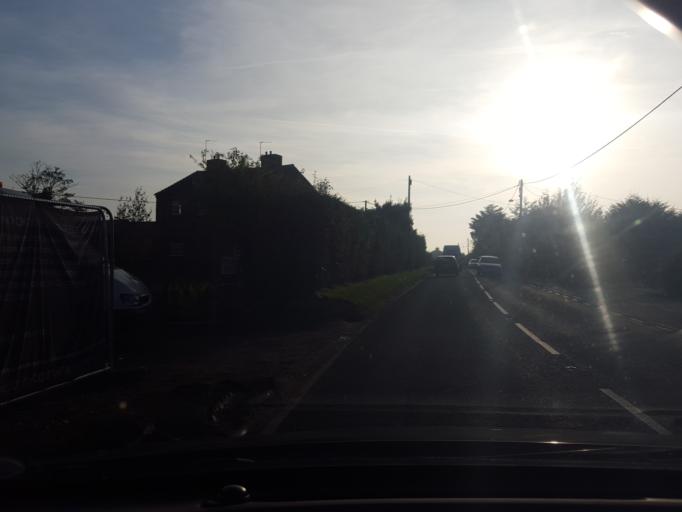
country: GB
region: England
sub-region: Essex
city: Frinton-on-Sea
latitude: 51.8356
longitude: 1.2131
